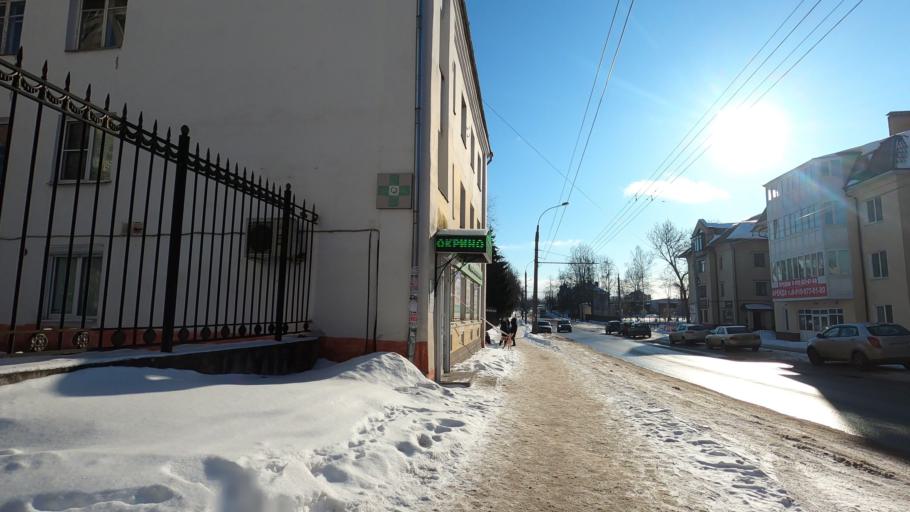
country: RU
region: Jaroslavl
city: Rybinsk
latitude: 58.0457
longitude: 38.8384
